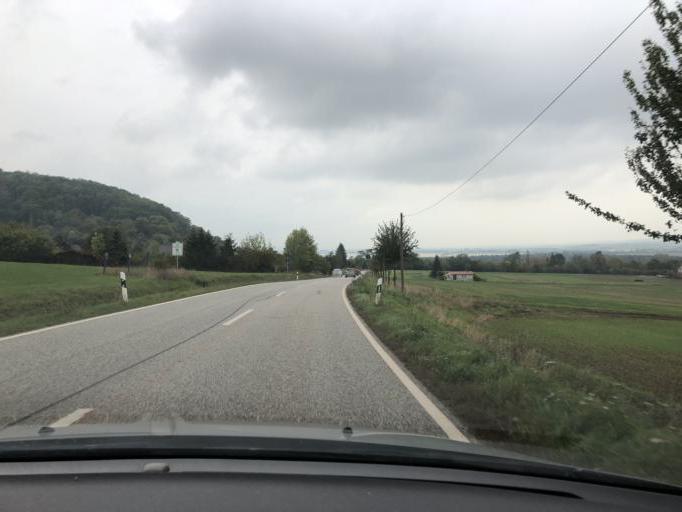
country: DE
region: Saxony-Anhalt
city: Kelbra
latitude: 51.4282
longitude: 11.0495
